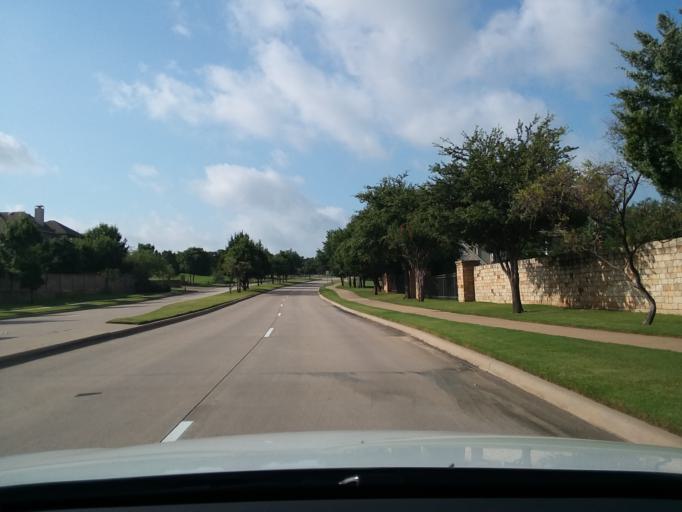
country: US
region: Texas
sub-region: Denton County
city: Bartonville
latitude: 33.0858
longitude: -97.1263
